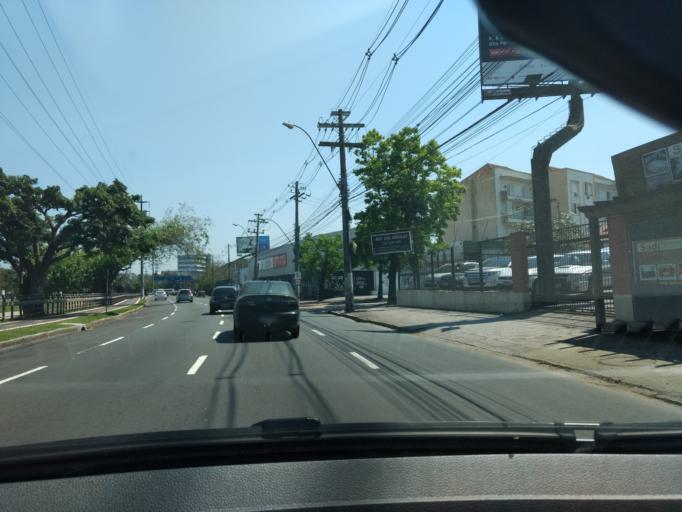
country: BR
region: Rio Grande do Sul
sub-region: Porto Alegre
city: Porto Alegre
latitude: -30.0432
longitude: -51.2006
